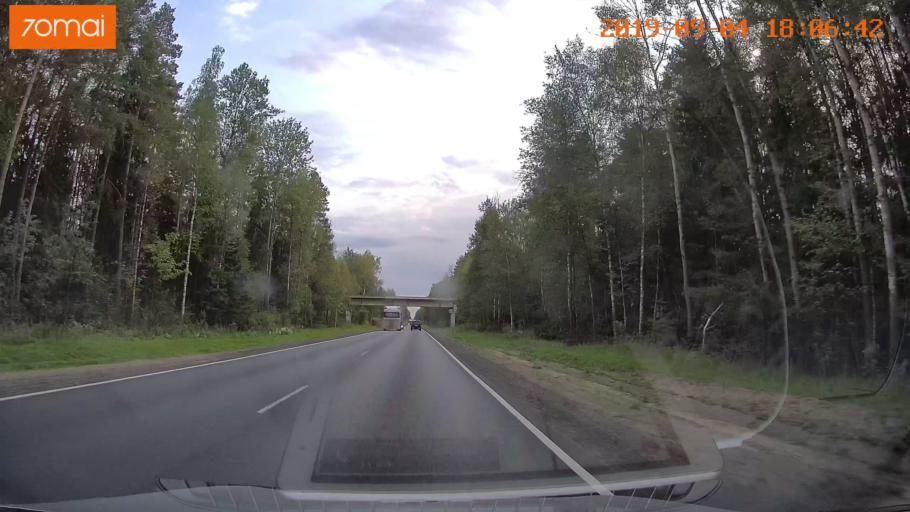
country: RU
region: Moskovskaya
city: Khorlovo
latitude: 55.4283
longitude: 38.8115
